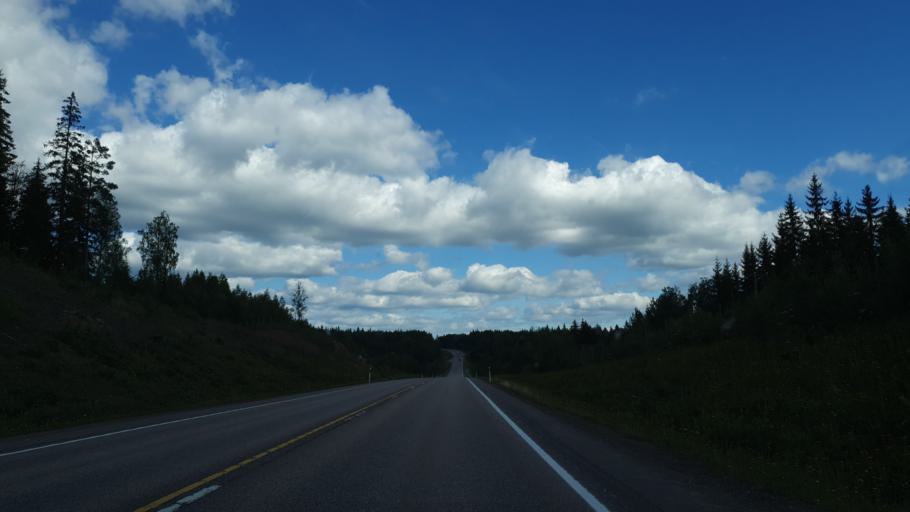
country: FI
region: Central Finland
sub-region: Jaemsae
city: Jaemsae
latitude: 61.8057
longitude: 24.9793
